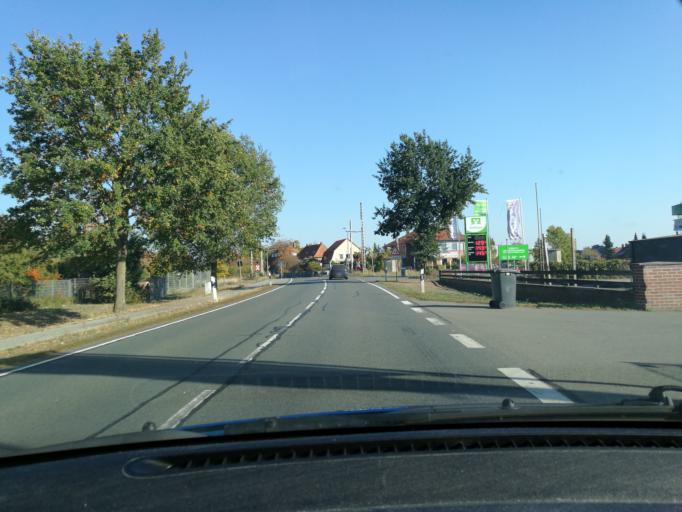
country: DE
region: Lower Saxony
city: Dannenberg
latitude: 53.0950
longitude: 11.0817
